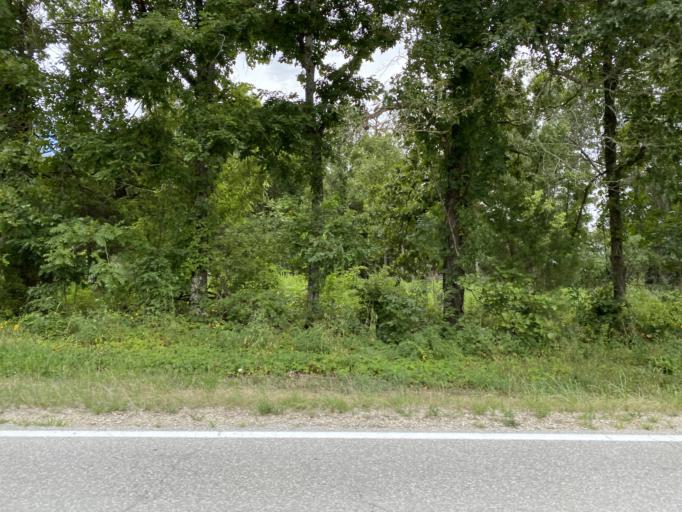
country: US
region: Arkansas
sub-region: Fulton County
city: Salem
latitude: 36.4185
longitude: -91.7184
